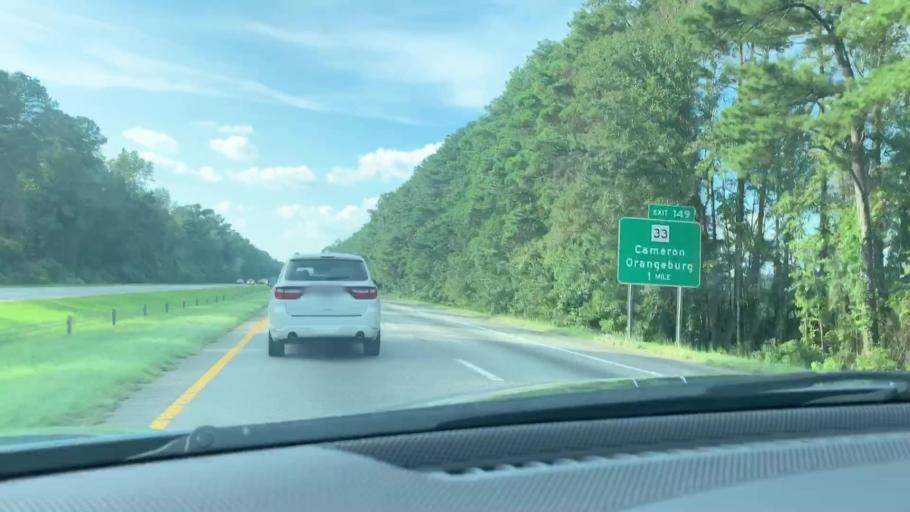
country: US
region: South Carolina
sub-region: Orangeburg County
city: Brookdale
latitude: 33.5094
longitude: -80.7796
